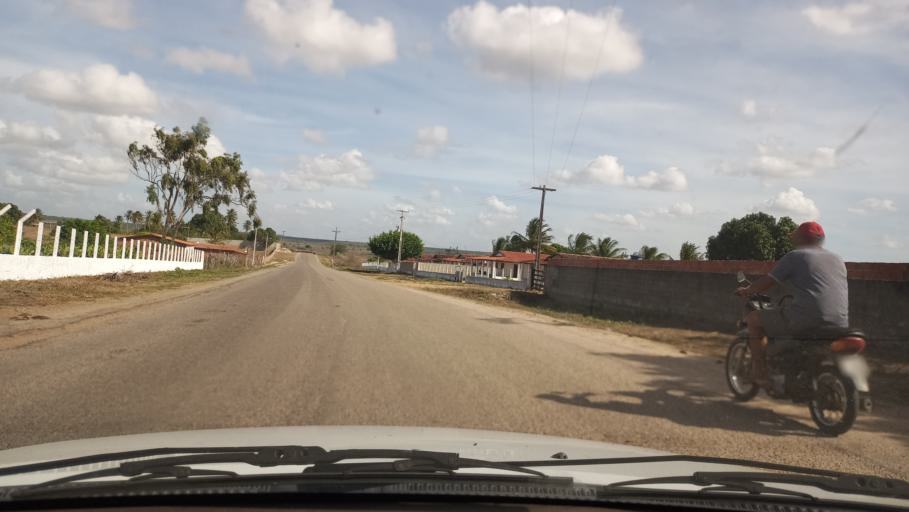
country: BR
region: Rio Grande do Norte
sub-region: Goianinha
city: Goianinha
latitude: -6.3218
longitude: -35.3073
